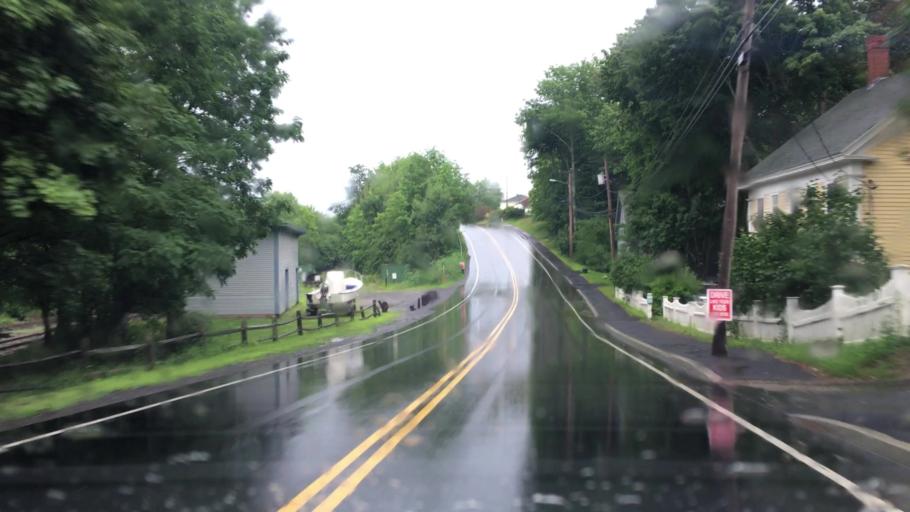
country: US
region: Maine
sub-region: Kennebec County
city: Randolph
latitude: 44.2272
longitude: -69.7690
